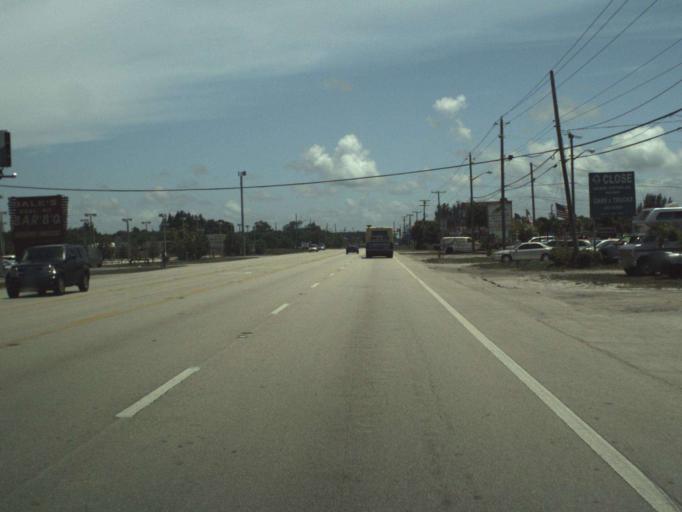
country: US
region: Florida
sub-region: Saint Lucie County
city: White City
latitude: 27.4006
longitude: -80.3259
